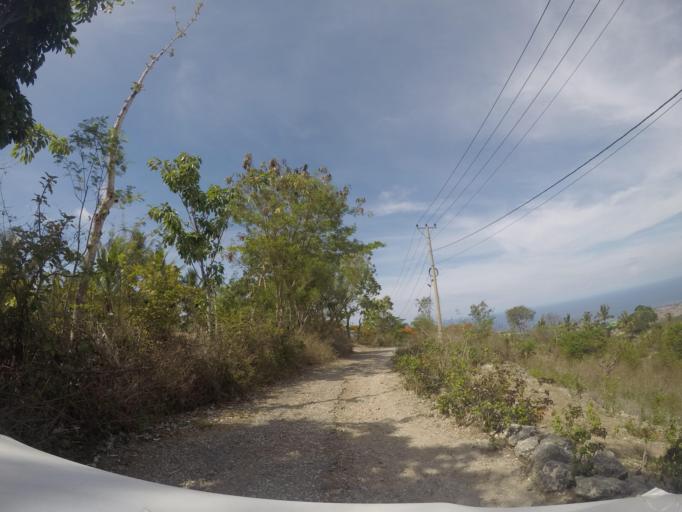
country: TL
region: Baucau
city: Baucau
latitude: -8.4692
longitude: 126.4653
